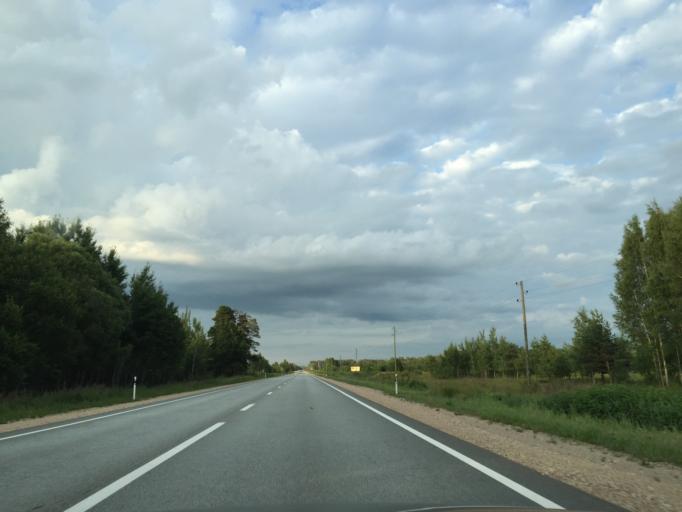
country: LV
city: Tireli
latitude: 56.8834
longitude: 23.6471
